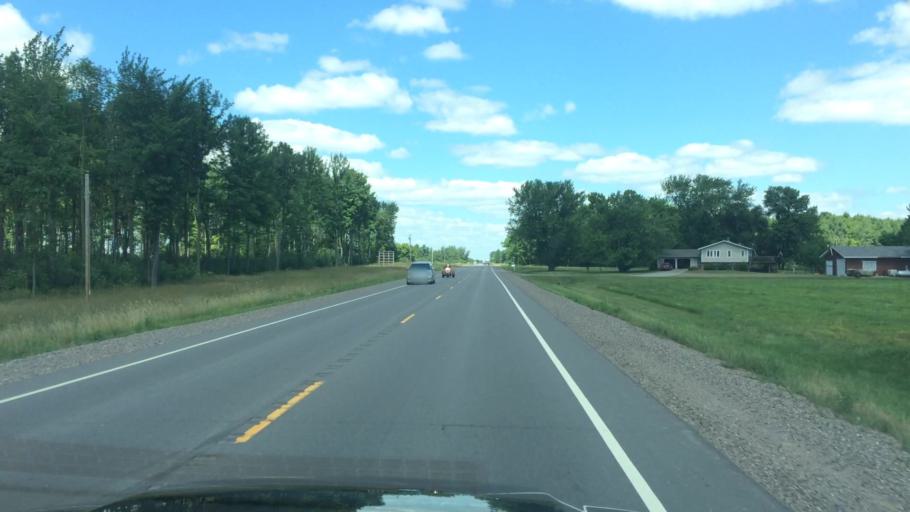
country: US
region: Wisconsin
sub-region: Clark County
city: Abbotsford
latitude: 45.0229
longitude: -90.3151
